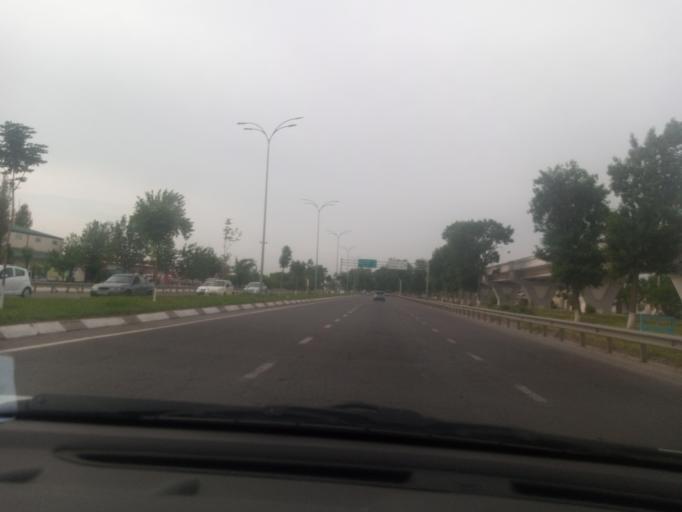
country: UZ
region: Toshkent Shahri
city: Bektemir
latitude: 41.2747
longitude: 69.3619
